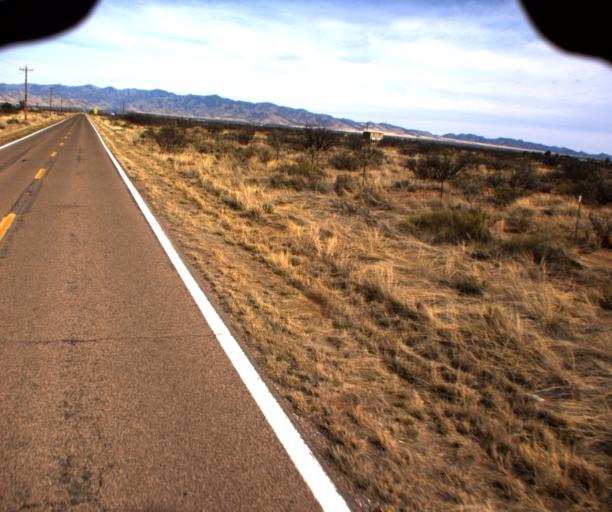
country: US
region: Arizona
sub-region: Cochise County
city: Willcox
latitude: 31.8762
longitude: -109.6054
